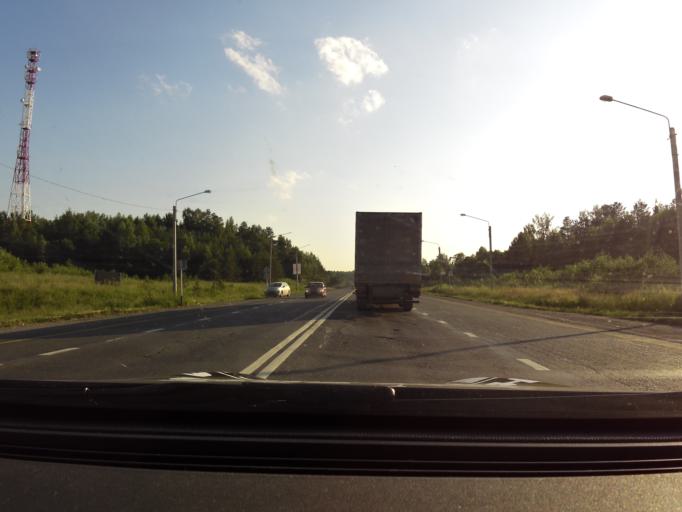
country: RU
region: Sverdlovsk
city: Druzhinino
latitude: 56.8051
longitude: 59.4829
